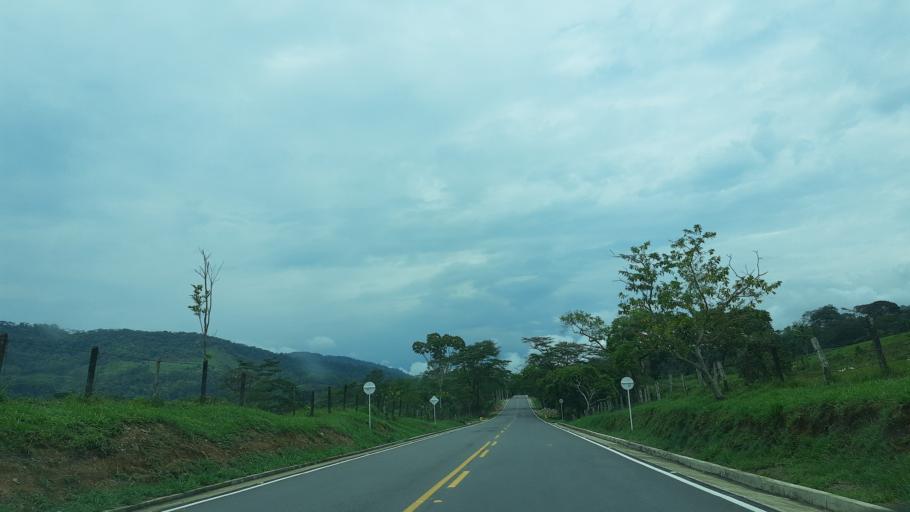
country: CO
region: Casanare
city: Sabanalarga
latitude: 4.8169
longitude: -73.0650
